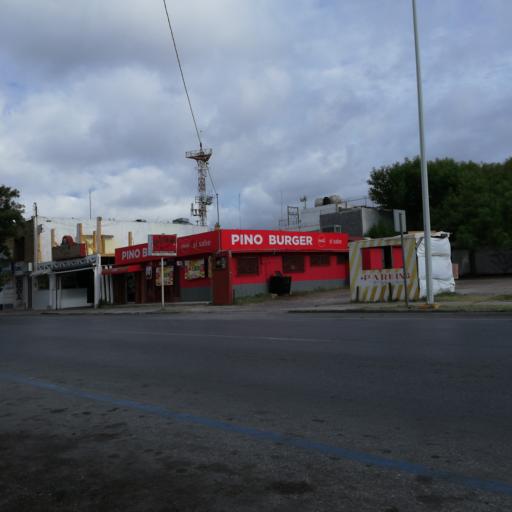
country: MX
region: Tamaulipas
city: Nuevo Laredo
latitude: 27.4861
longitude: -99.5042
